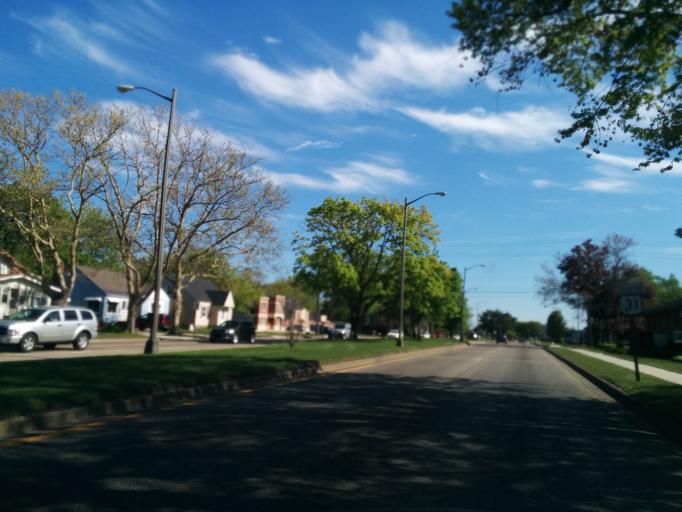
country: US
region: Michigan
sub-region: Ottawa County
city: Grand Haven
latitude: 43.0572
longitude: -86.2210
